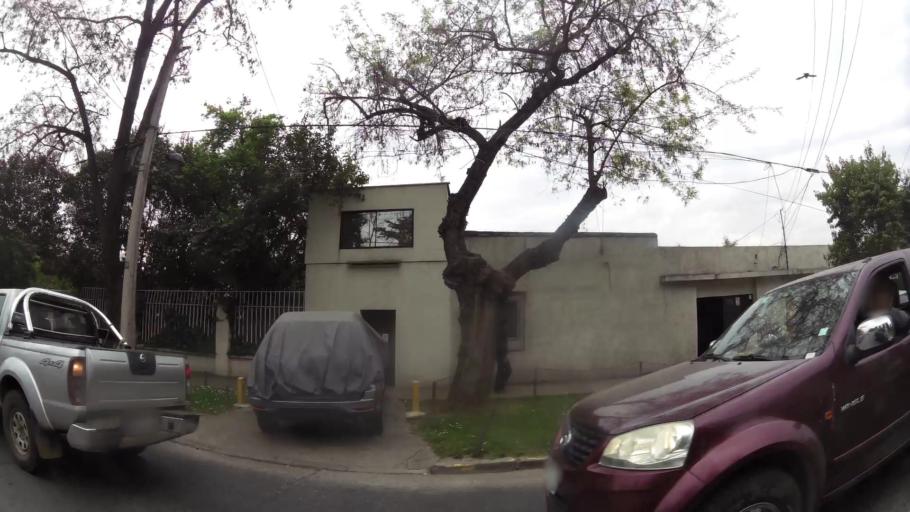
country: CL
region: Santiago Metropolitan
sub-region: Provincia de Santiago
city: Villa Presidente Frei, Nunoa, Santiago, Chile
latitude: -33.4741
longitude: -70.6054
